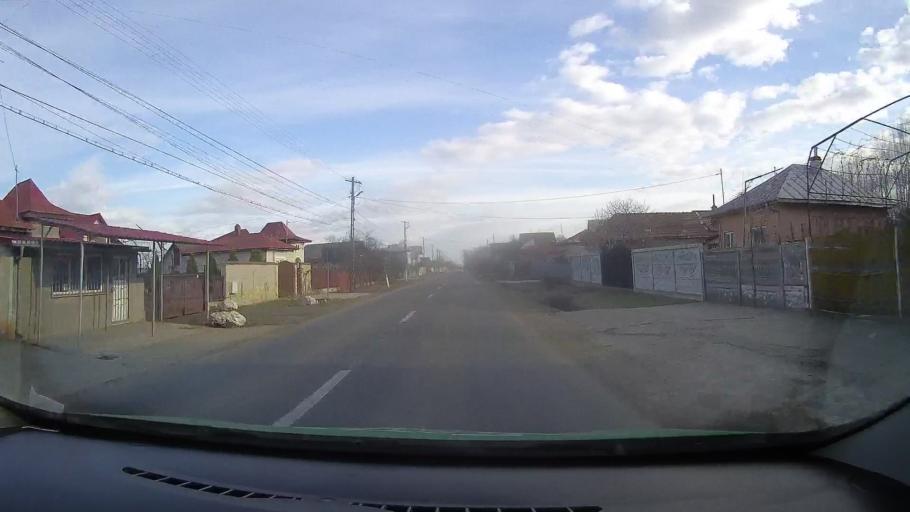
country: RO
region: Dambovita
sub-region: Comuna Vacaresti
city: Vacaresti
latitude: 44.8619
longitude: 25.4787
